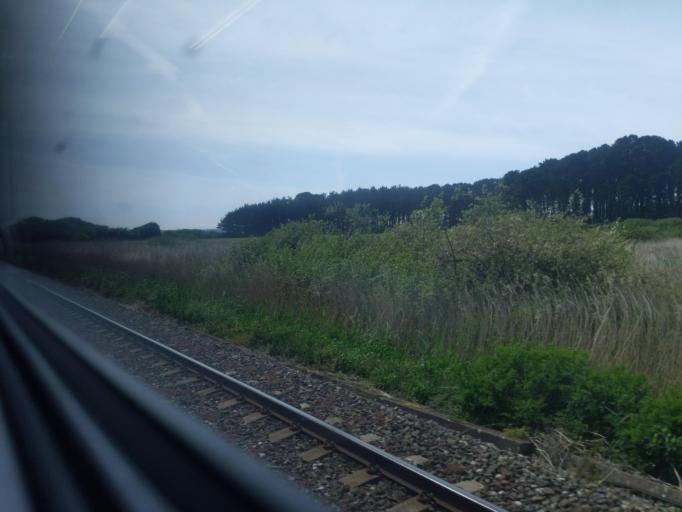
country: GB
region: England
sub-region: Cornwall
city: Marazion
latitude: 50.1320
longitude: -5.4825
